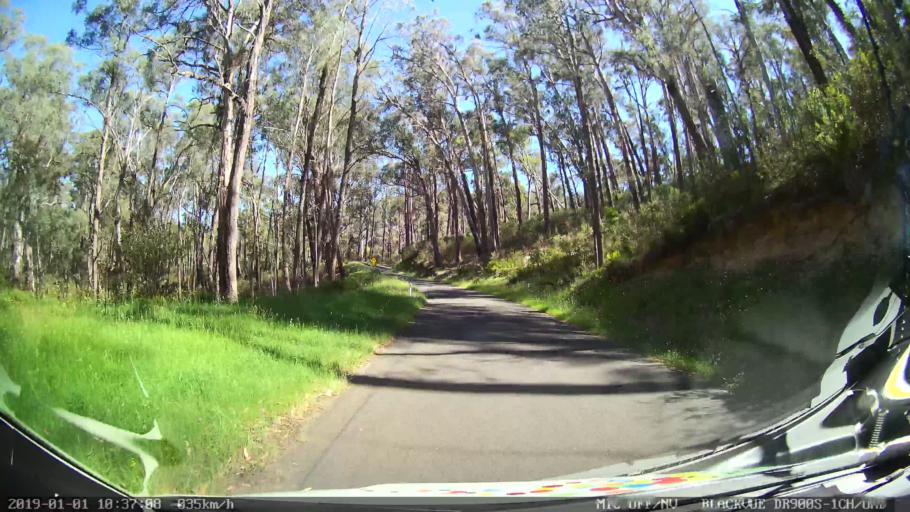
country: AU
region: New South Wales
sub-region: Snowy River
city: Jindabyne
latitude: -36.0502
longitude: 148.3039
